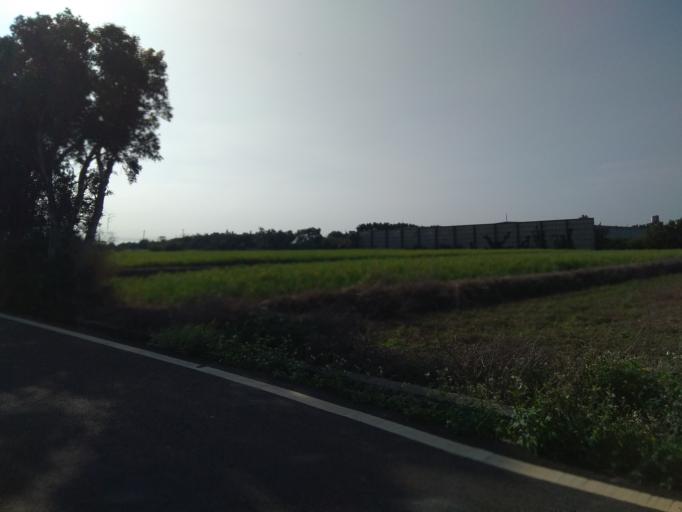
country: TW
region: Taiwan
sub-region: Hsinchu
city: Zhubei
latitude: 25.0046
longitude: 121.0455
